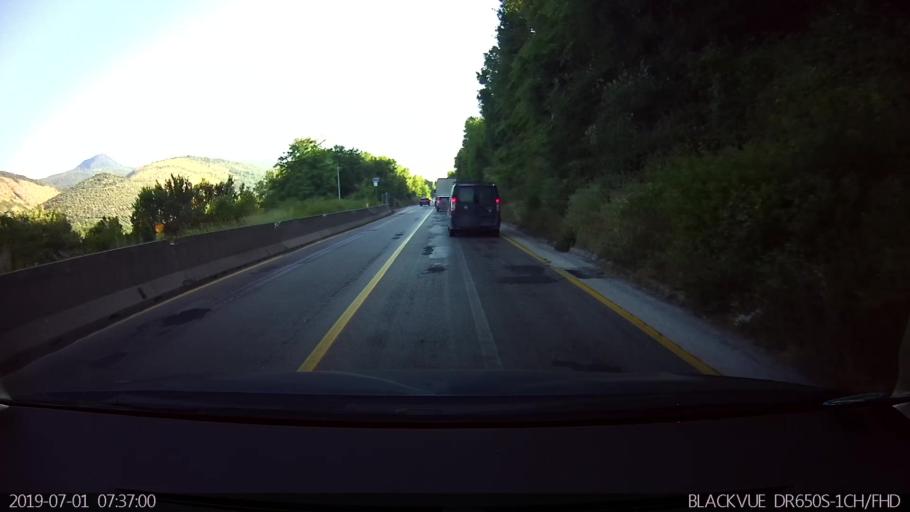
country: IT
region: Latium
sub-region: Provincia di Frosinone
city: Giuliano di Roma
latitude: 41.5350
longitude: 13.2666
